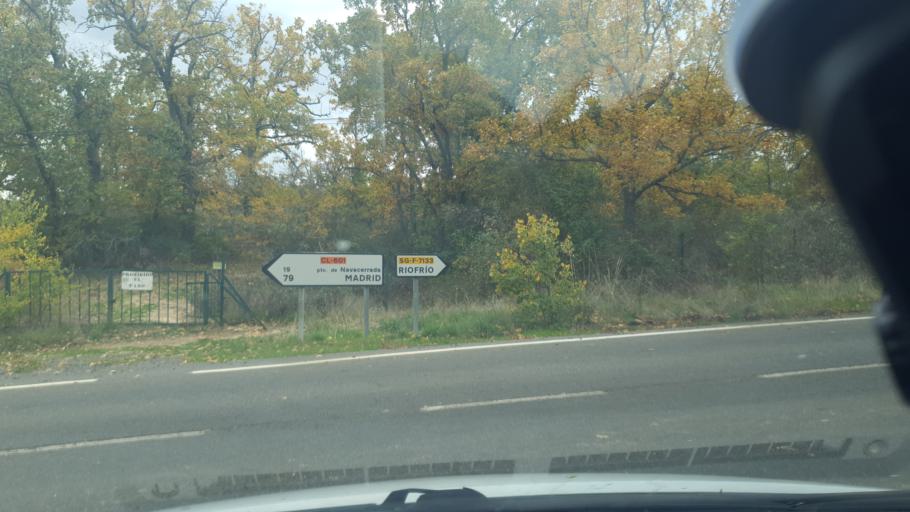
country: ES
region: Castille and Leon
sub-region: Provincia de Segovia
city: San Ildefonso
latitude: 40.9042
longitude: -4.0354
